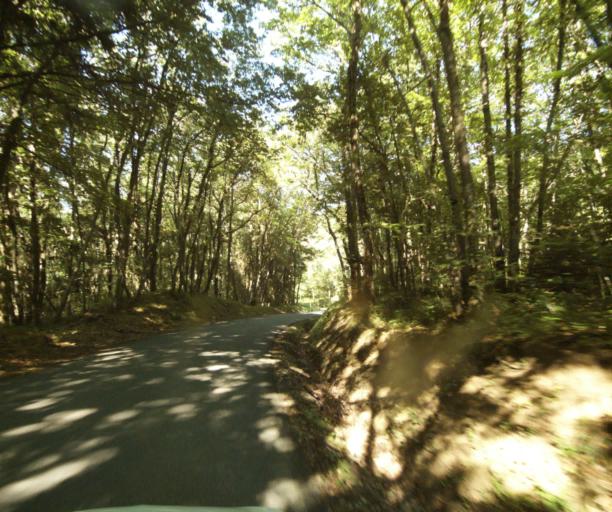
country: FR
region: Rhone-Alpes
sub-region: Departement de la Haute-Savoie
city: Massongy
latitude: 46.3093
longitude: 6.3451
